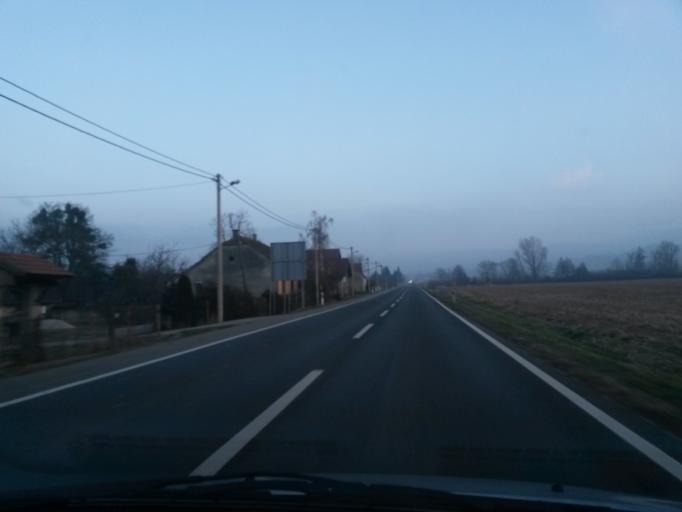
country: HR
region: Koprivnicko-Krizevacka
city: Reka
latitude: 46.1972
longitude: 16.7210
